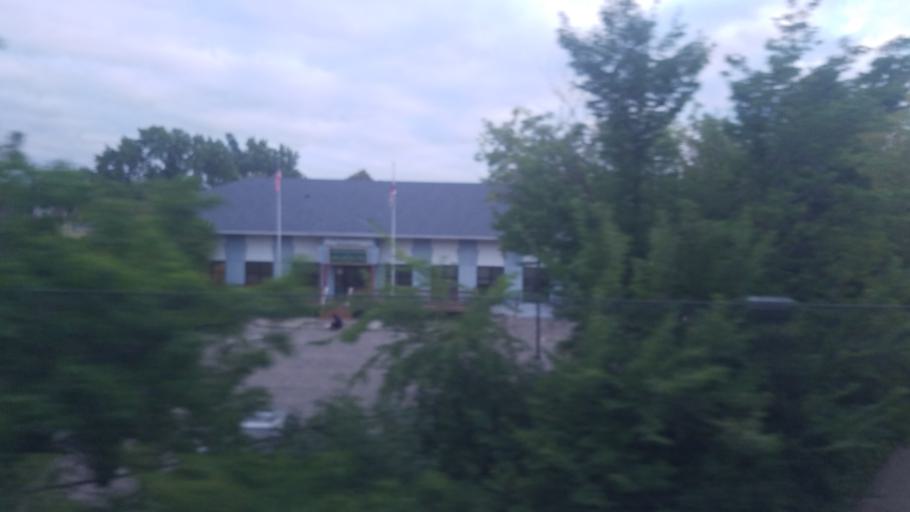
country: US
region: Minnesota
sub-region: Ramsey County
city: Lauderdale
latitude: 44.9748
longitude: -93.1937
